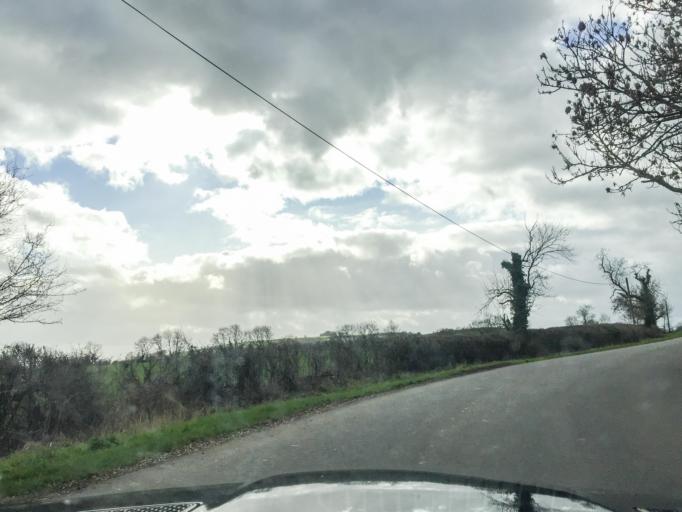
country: GB
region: England
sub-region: Oxfordshire
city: Hook Norton
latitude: 52.0644
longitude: -1.5370
